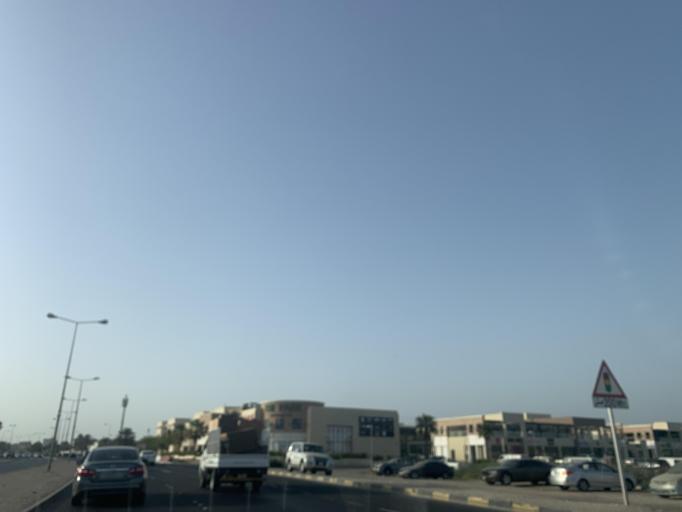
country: BH
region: Northern
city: Madinat `Isa
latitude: 26.1891
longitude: 50.4657
